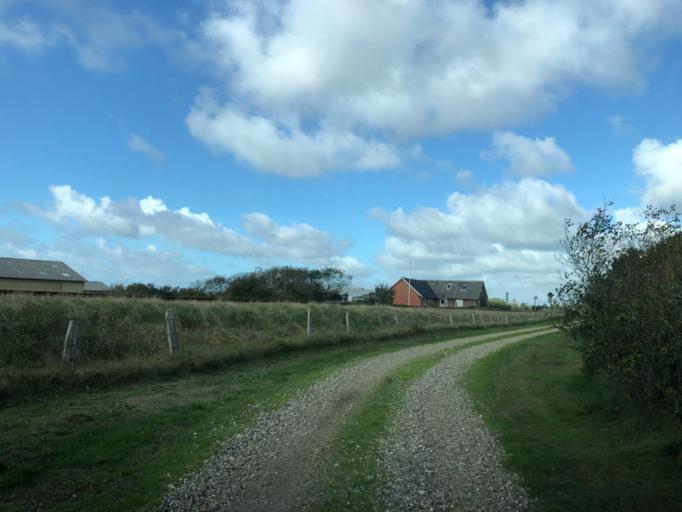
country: DK
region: Central Jutland
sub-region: Holstebro Kommune
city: Ulfborg
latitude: 56.2877
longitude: 8.3295
